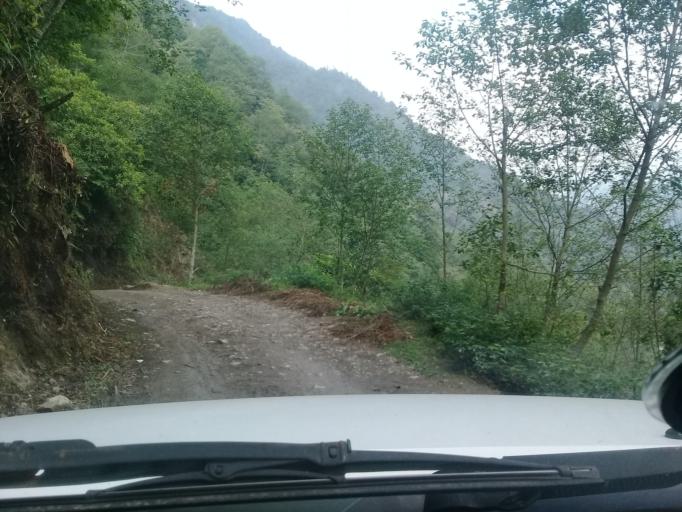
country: MX
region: Veracruz
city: La Perla
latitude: 18.9450
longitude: -97.1587
